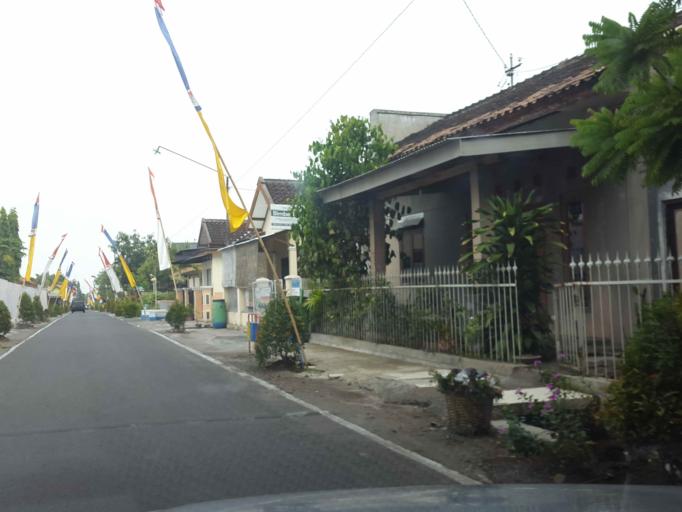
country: ID
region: Central Java
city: Jaten
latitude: -7.5952
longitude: 110.9476
